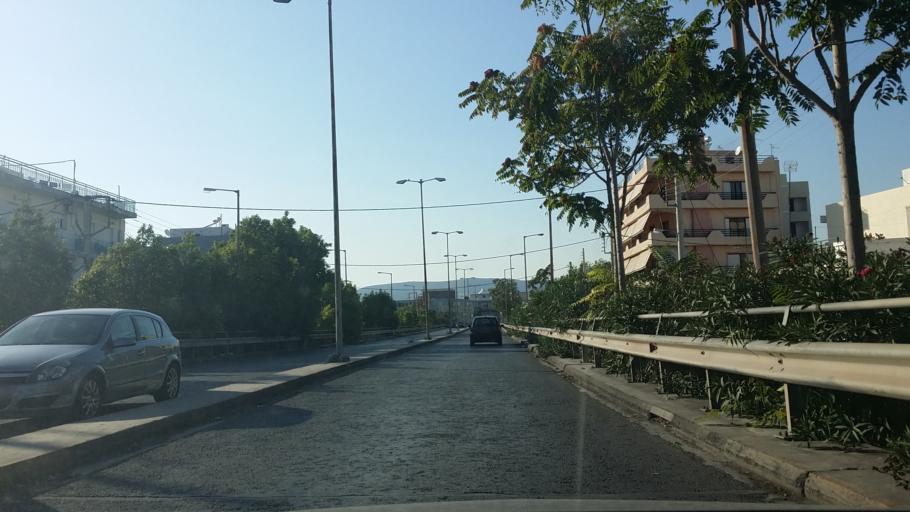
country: GR
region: Attica
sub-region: Nomarchia Athinas
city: Agioi Anargyroi
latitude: 38.0154
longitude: 23.7141
